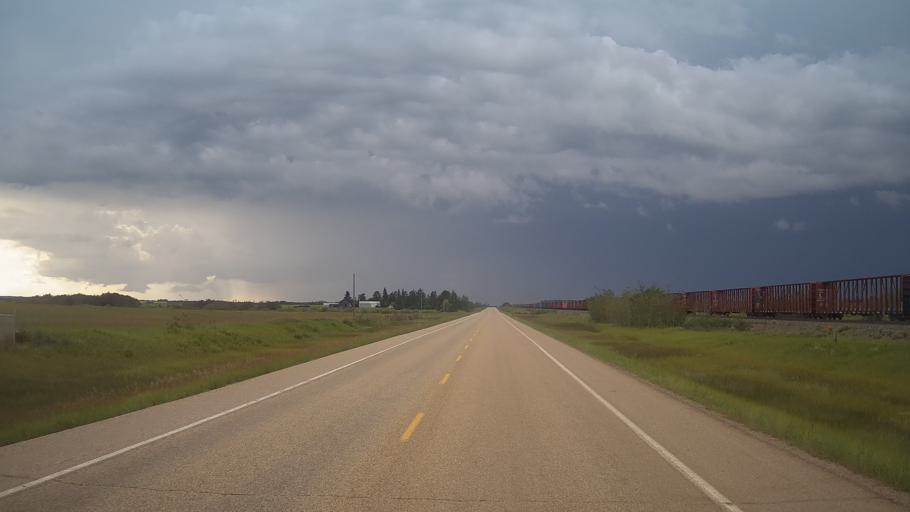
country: CA
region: Alberta
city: Tofield
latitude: 53.2695
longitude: -112.3688
